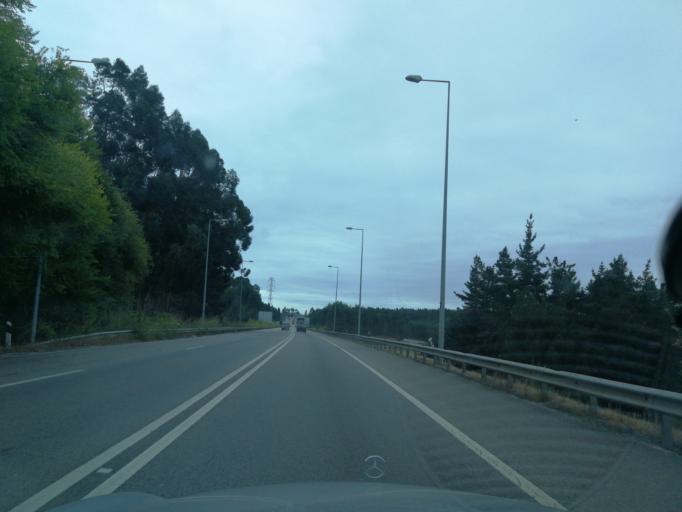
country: PT
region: Aveiro
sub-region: Agueda
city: Valongo
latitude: 40.6070
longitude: -8.4667
